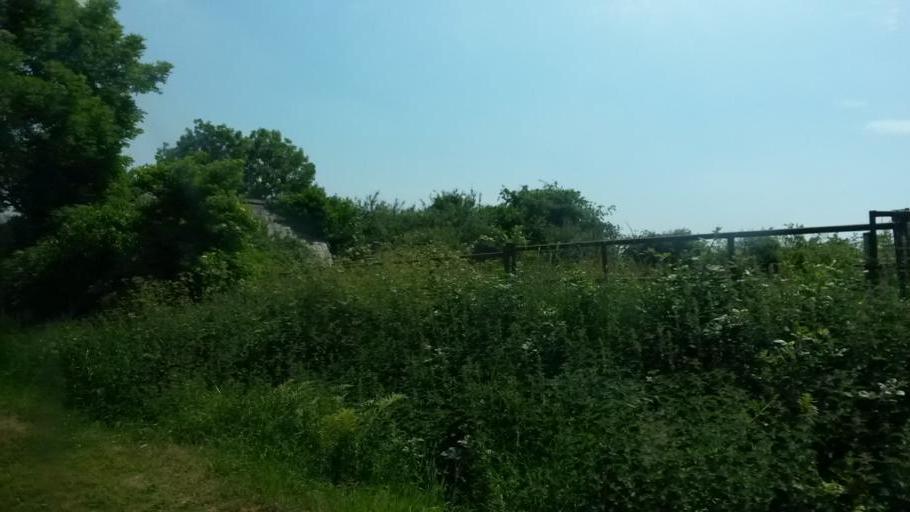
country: IE
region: Leinster
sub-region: An Mhi
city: Slane
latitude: 53.7165
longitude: -6.5382
